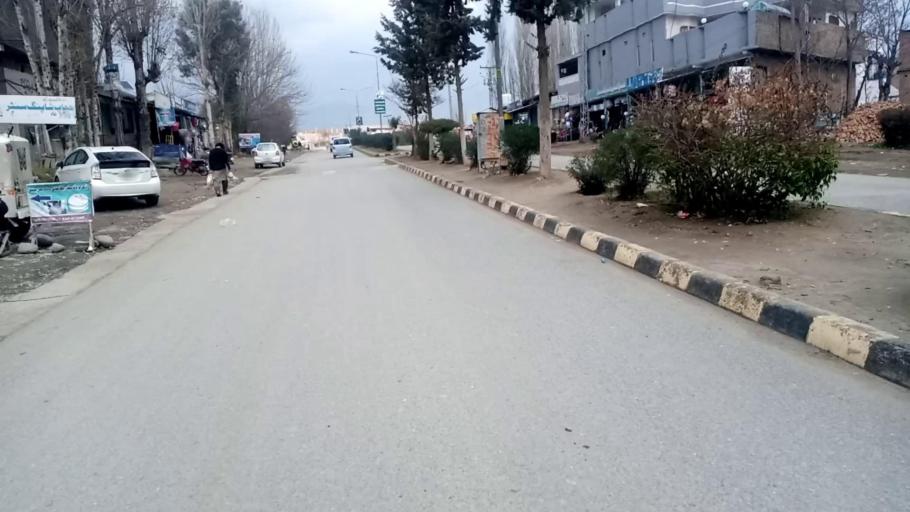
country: PK
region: Khyber Pakhtunkhwa
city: Mingora
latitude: 34.8101
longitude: 72.3408
